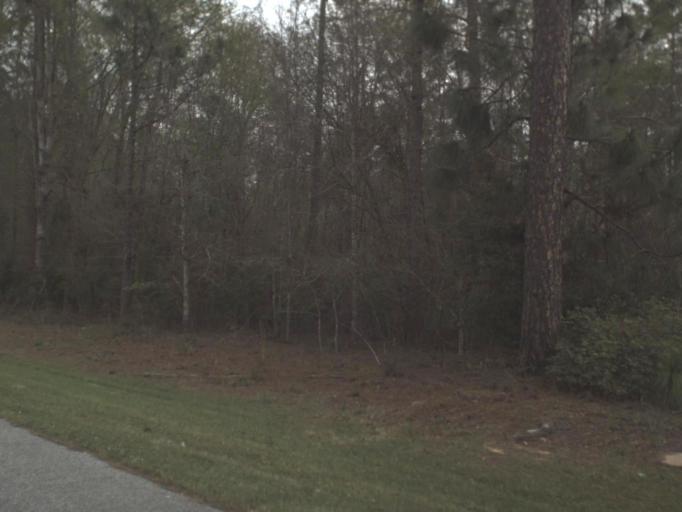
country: US
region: Florida
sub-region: Holmes County
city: Bonifay
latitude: 30.8322
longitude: -85.6670
